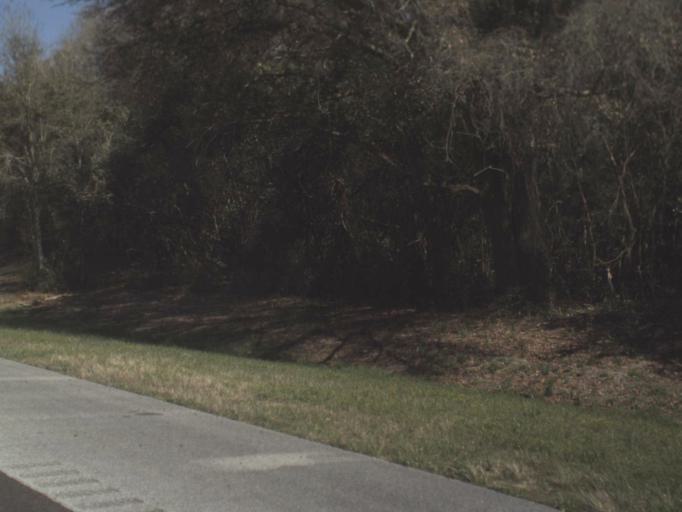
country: US
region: Florida
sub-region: Walton County
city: DeFuniak Springs
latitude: 30.7414
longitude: -86.2280
